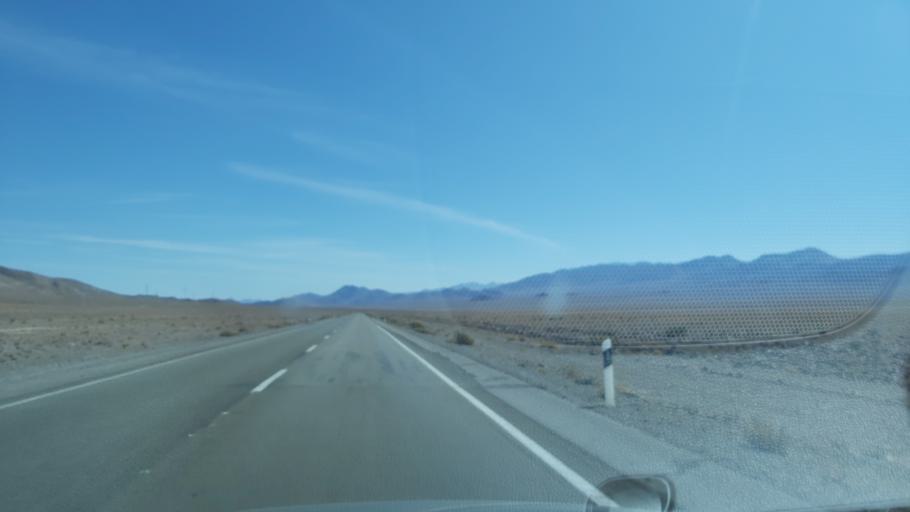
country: CL
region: Atacama
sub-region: Provincia de Chanaral
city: Diego de Almagro
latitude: -26.8677
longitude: -69.9070
